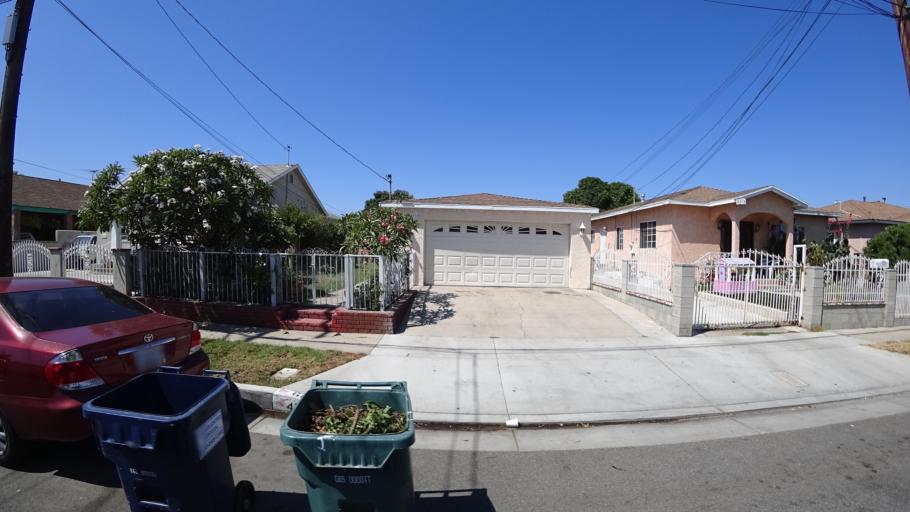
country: US
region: California
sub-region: Los Angeles County
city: Lennox
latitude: 33.9409
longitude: -118.3510
